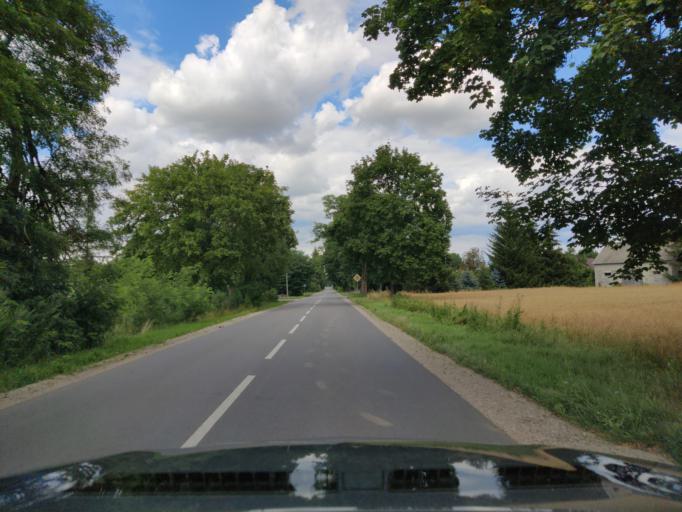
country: PL
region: Masovian Voivodeship
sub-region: Powiat wegrowski
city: Miedzna
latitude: 52.5413
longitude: 22.0919
